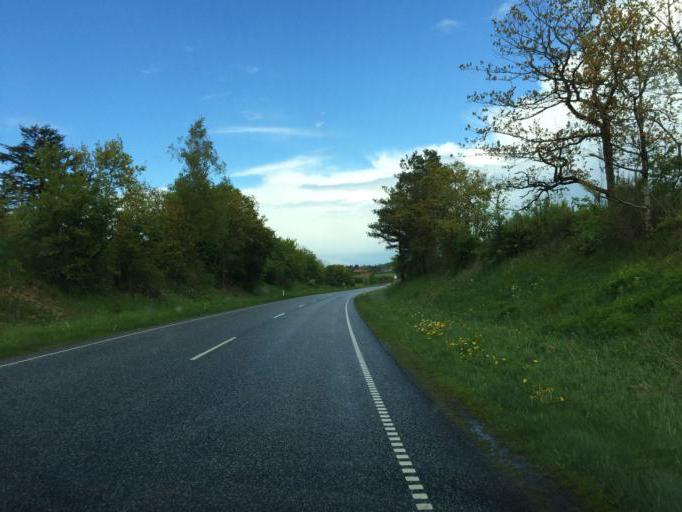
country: DK
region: North Denmark
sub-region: Vesthimmerland Kommune
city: Farso
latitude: 56.6187
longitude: 9.3489
